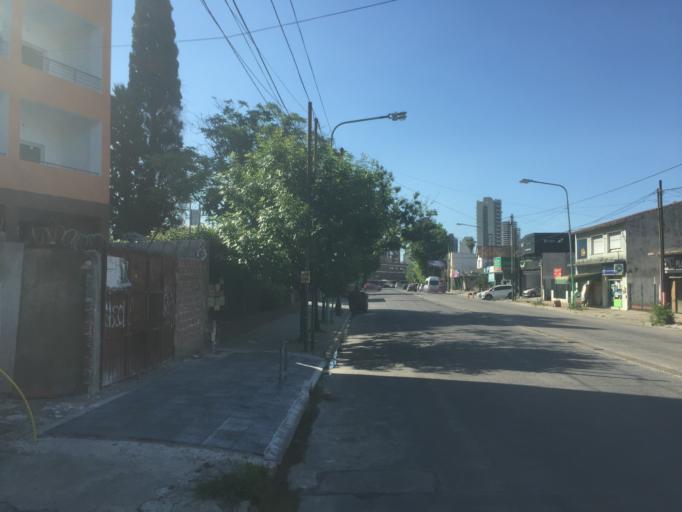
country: AR
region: Buenos Aires
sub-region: Partido de Lomas de Zamora
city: Lomas de Zamora
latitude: -34.7721
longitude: -58.3952
